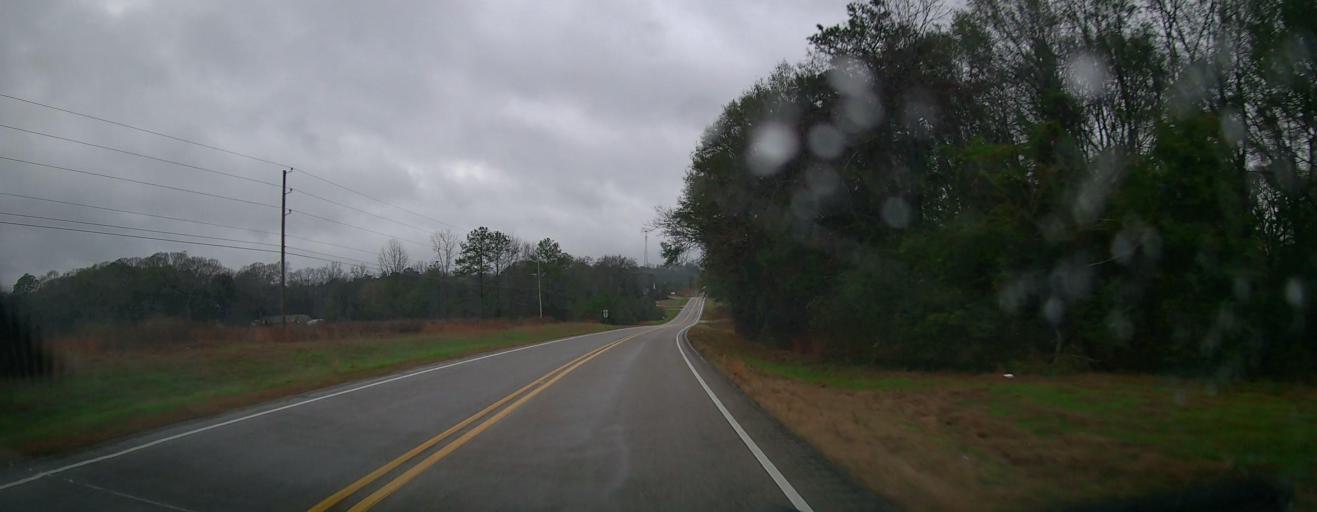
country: US
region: Alabama
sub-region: Autauga County
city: Pine Level
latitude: 32.5343
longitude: -86.6391
